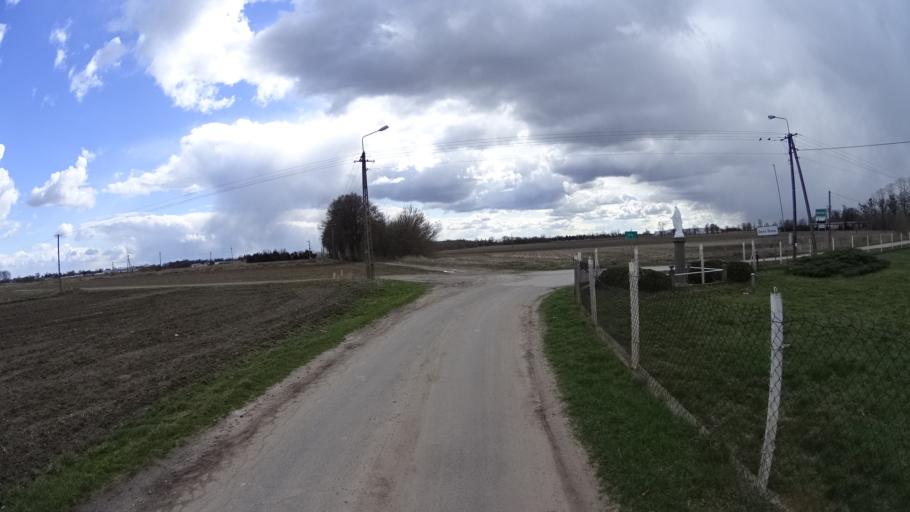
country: PL
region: Masovian Voivodeship
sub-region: Powiat warszawski zachodni
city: Jozefow
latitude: 52.2205
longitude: 20.6774
